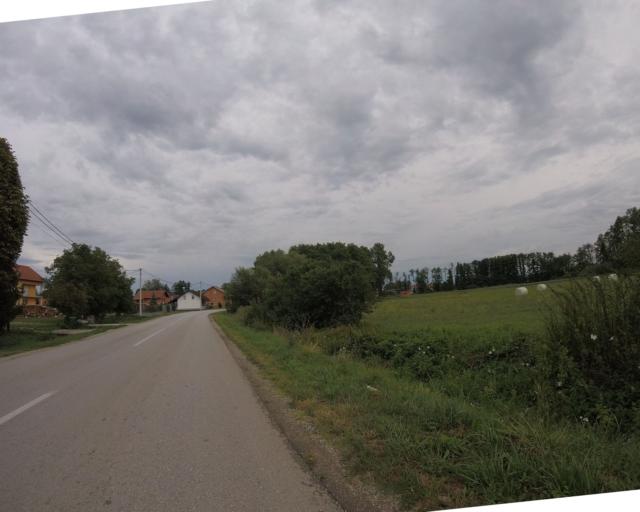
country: HR
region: Zagrebacka
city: Kuce
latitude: 45.7098
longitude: 16.1612
